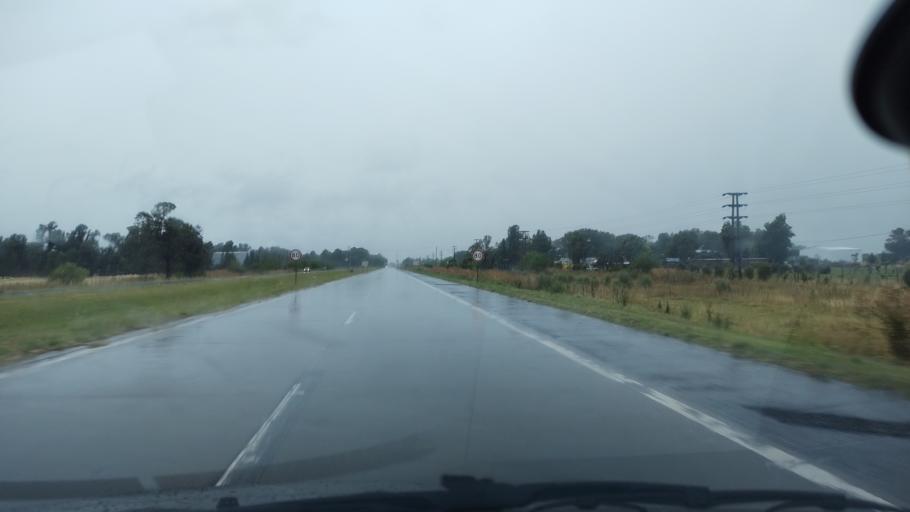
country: AR
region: Buenos Aires
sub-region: Partido de San Vicente
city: San Vicente
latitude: -35.0582
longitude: -58.4499
